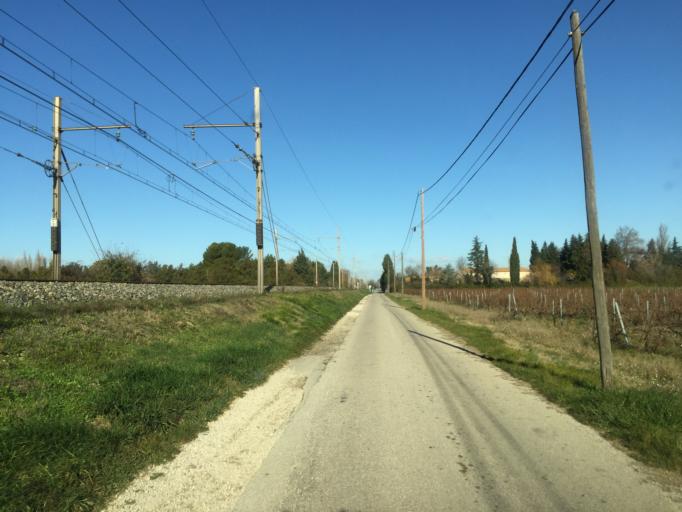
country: FR
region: Provence-Alpes-Cote d'Azur
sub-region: Departement du Vaucluse
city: Courthezon
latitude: 44.0768
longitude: 4.8904
